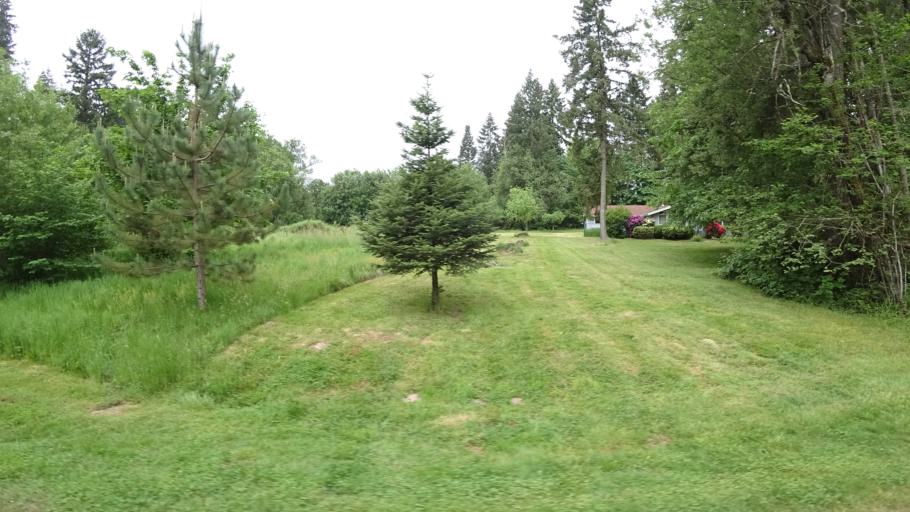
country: US
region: Oregon
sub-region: Washington County
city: Rockcreek
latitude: 45.5742
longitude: -122.8956
